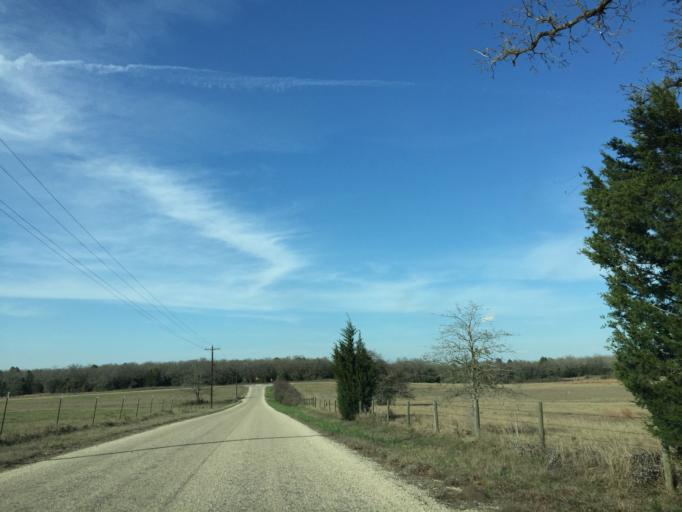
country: US
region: Texas
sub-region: Milam County
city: Thorndale
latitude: 30.4572
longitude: -97.1915
